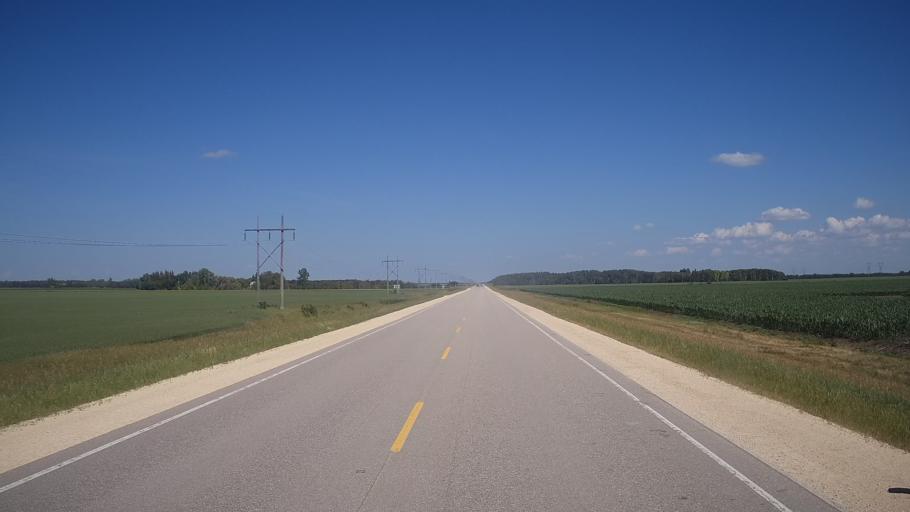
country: CA
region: Manitoba
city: Stonewall
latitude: 50.1227
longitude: -97.4669
